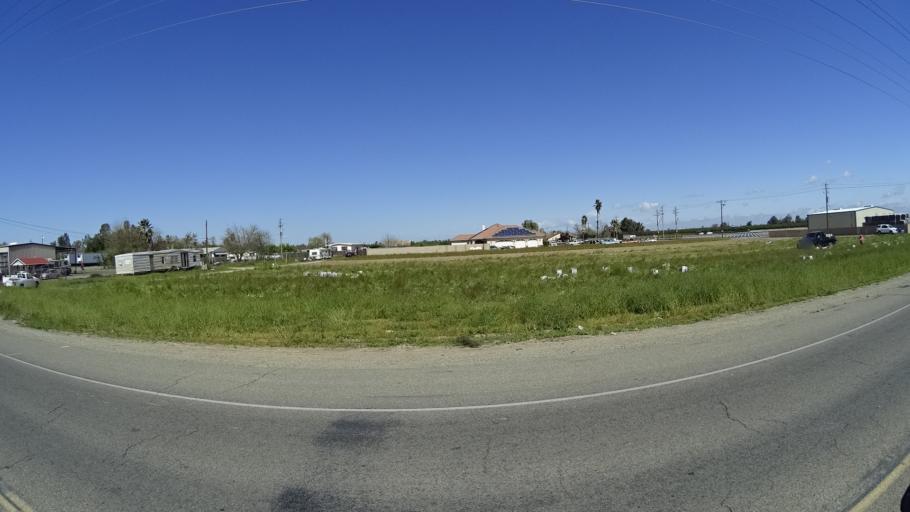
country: US
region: California
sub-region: Fresno County
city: West Park
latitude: 36.7065
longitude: -119.8454
